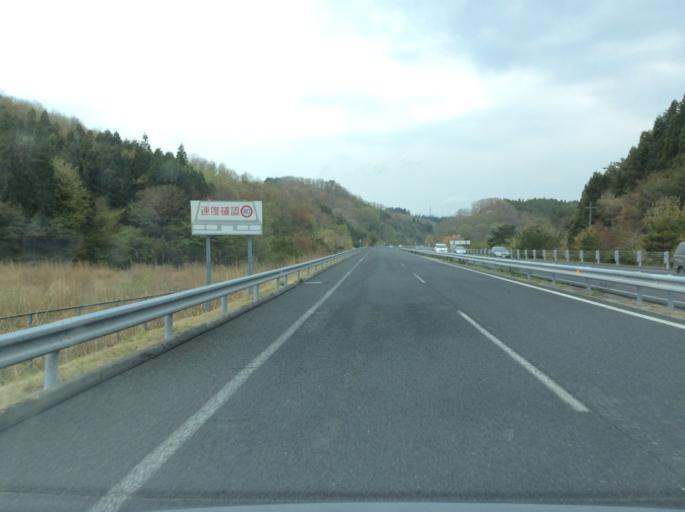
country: JP
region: Fukushima
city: Iwaki
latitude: 37.1970
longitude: 140.7014
